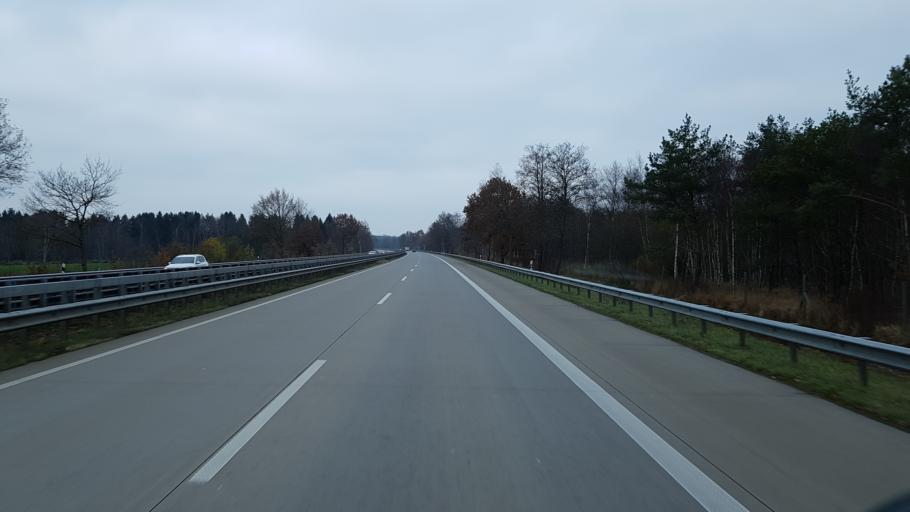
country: DE
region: Lower Saxony
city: Schwanewede
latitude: 53.2661
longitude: 8.6362
